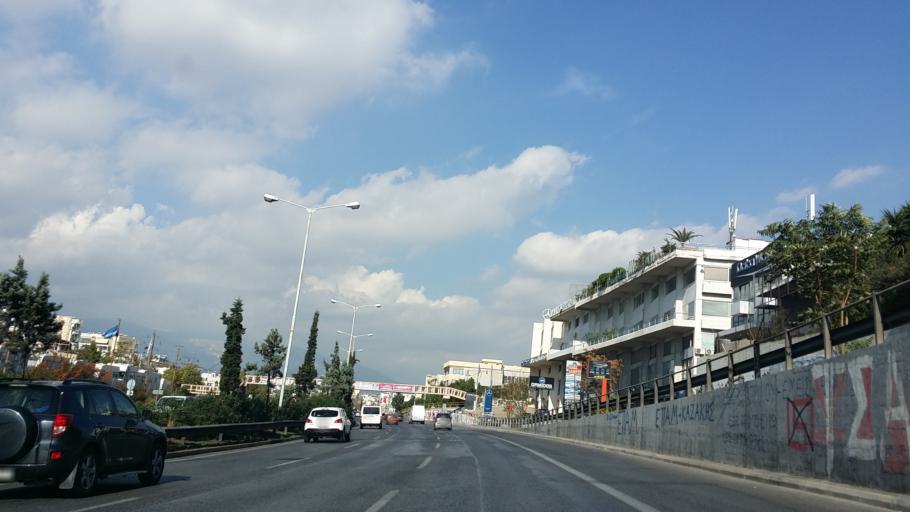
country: GR
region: Attica
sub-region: Nomarchia Athinas
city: Nea Filadelfeia
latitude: 38.0379
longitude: 23.7338
